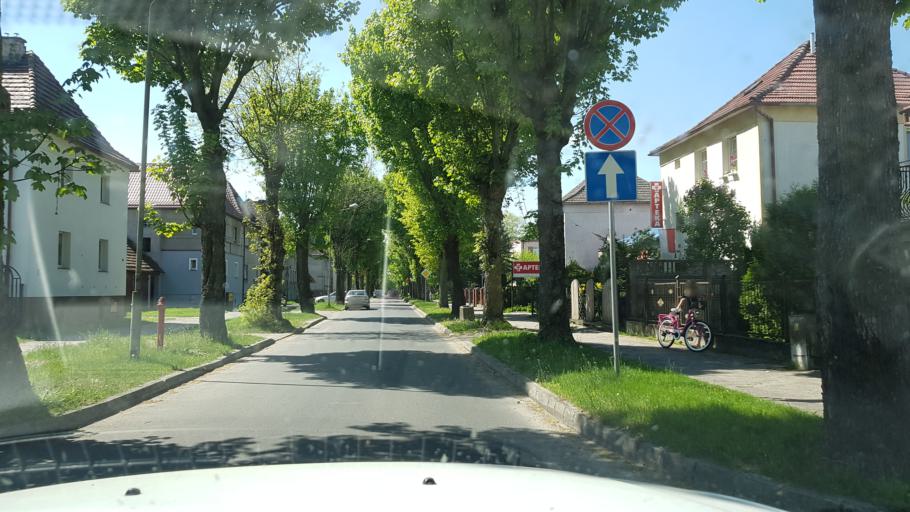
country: PL
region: West Pomeranian Voivodeship
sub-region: Powiat bialogardzki
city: Bialogard
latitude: 54.0077
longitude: 16.0046
